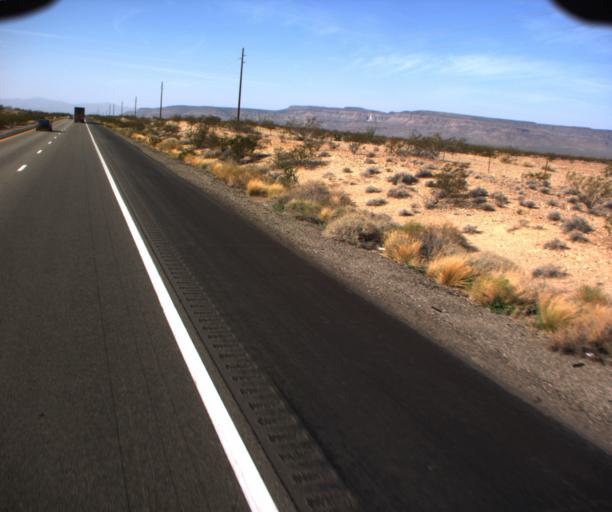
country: US
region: Arizona
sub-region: Mohave County
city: Kingman
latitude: 34.9741
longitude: -114.1419
